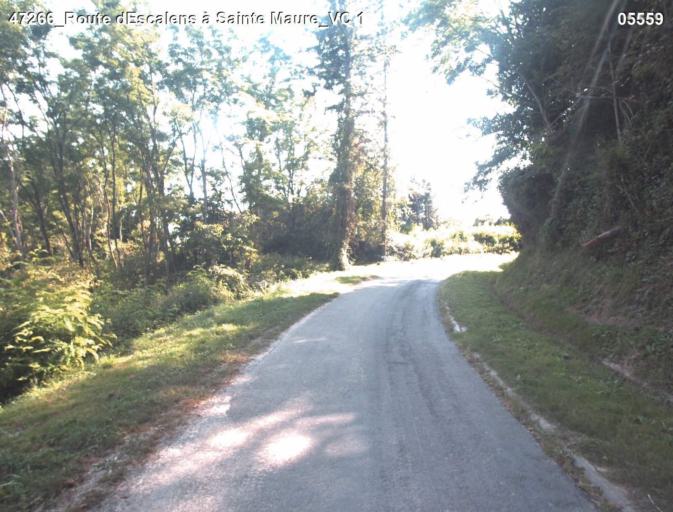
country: FR
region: Midi-Pyrenees
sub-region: Departement du Gers
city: Montreal
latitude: 44.0139
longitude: 0.1226
